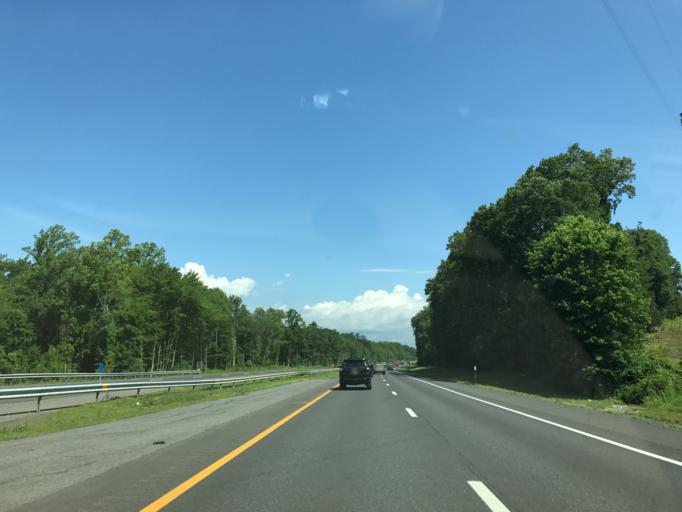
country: US
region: New York
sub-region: Ulster County
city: Tillson
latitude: 41.8192
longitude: -74.0566
